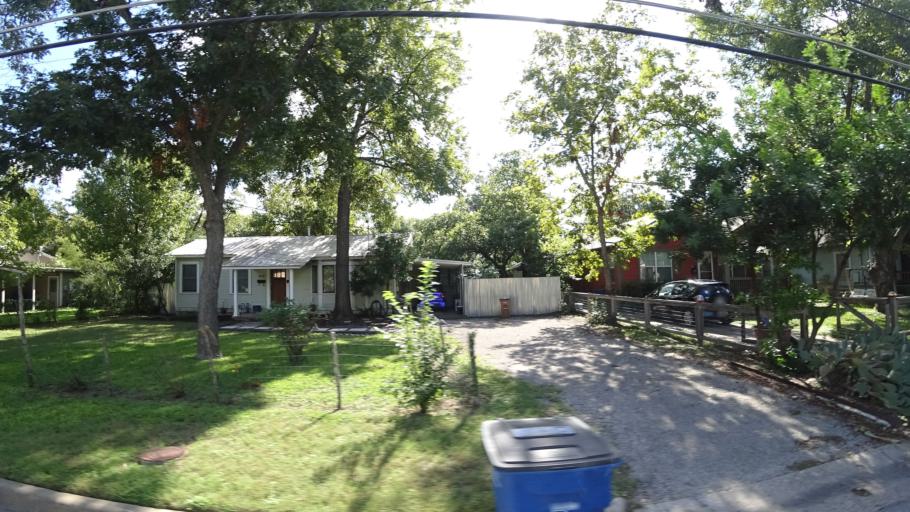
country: US
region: Texas
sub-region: Travis County
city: Austin
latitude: 30.3130
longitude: -97.7129
